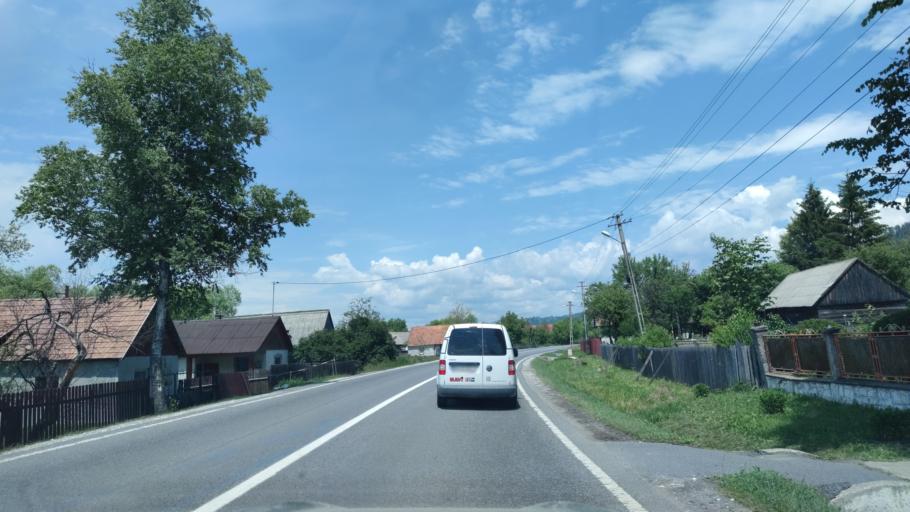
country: RO
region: Harghita
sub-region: Comuna Voslobeni
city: Voslobeni
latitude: 46.6332
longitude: 25.6228
